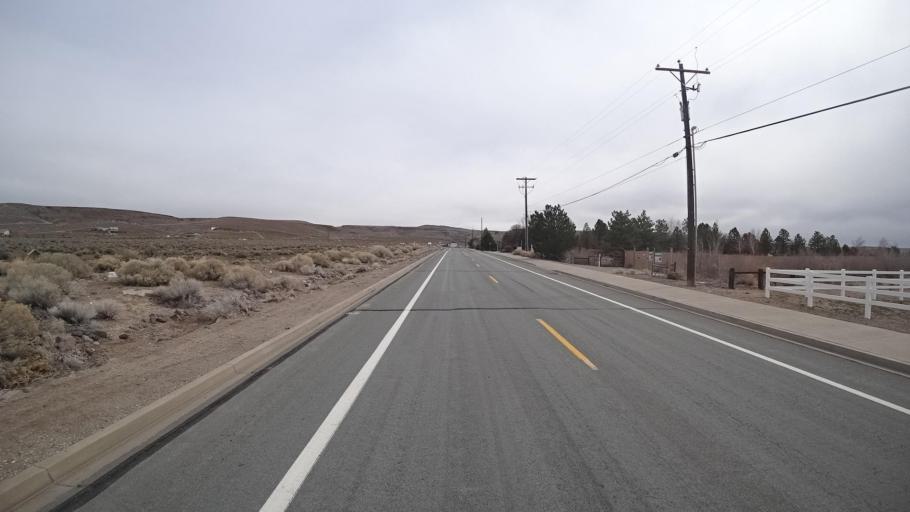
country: US
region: Nevada
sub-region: Washoe County
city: Spanish Springs
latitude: 39.6363
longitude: -119.6669
